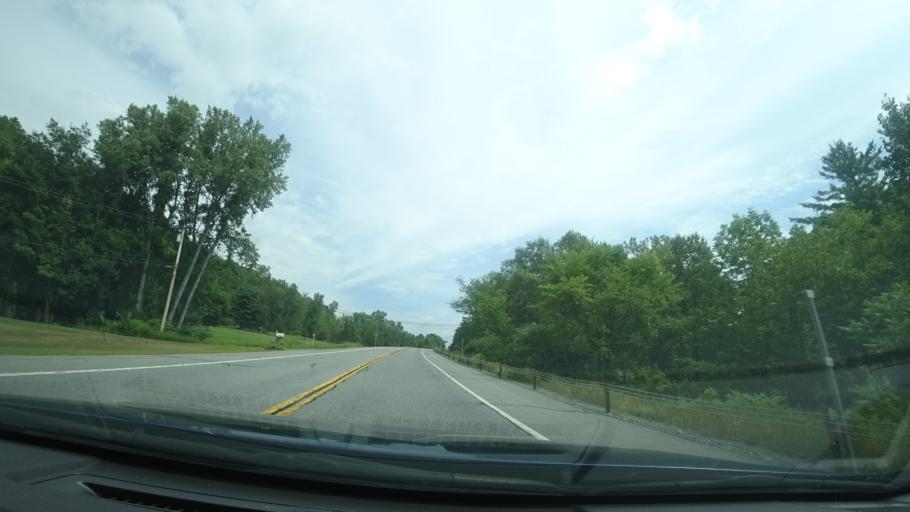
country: US
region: New York
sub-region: Washington County
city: Whitehall
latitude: 43.6695
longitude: -73.4172
